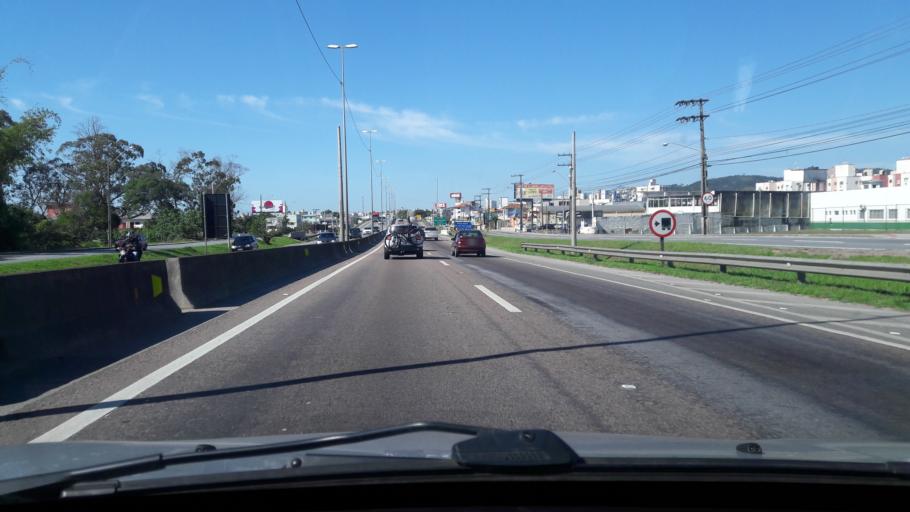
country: BR
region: Santa Catarina
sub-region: Sao Jose
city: Campinas
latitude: -27.5493
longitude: -48.6197
